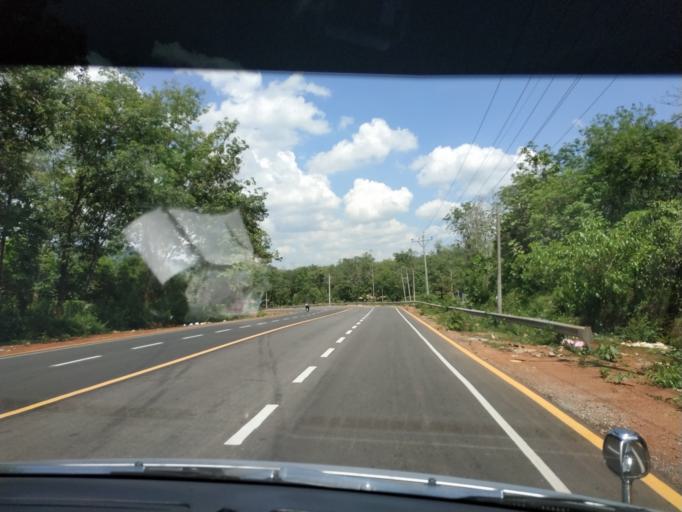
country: MM
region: Mon
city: Kyaikto
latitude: 17.3900
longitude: 97.0676
